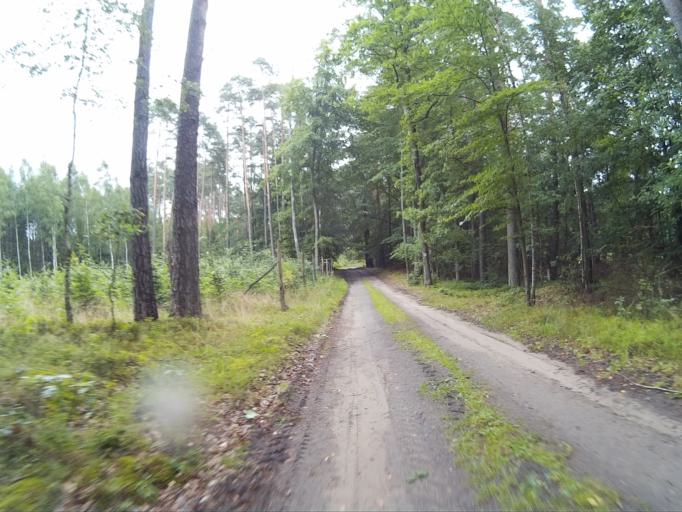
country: PL
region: Kujawsko-Pomorskie
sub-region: Powiat swiecki
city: Osie
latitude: 53.6358
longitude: 18.3775
